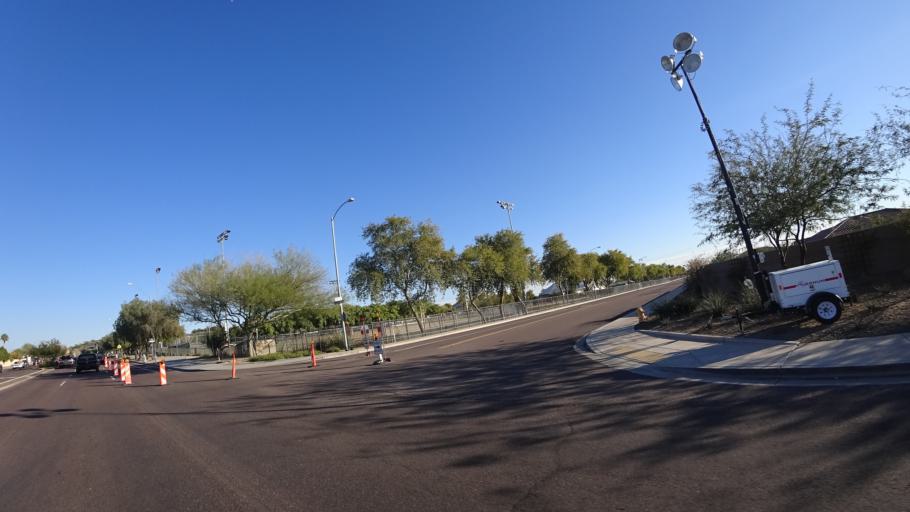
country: US
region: Arizona
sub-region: Maricopa County
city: Sun City
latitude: 33.7107
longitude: -112.2143
